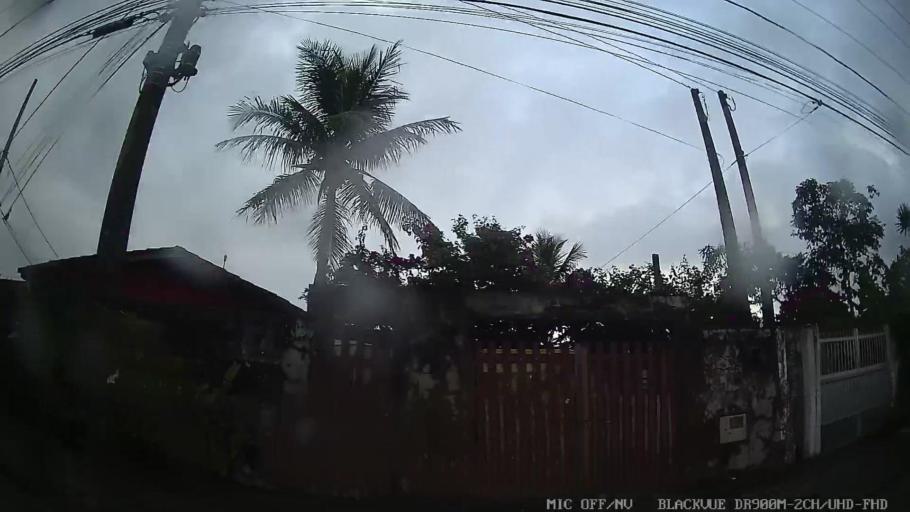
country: BR
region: Sao Paulo
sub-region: Itanhaem
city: Itanhaem
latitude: -24.1686
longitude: -46.7678
